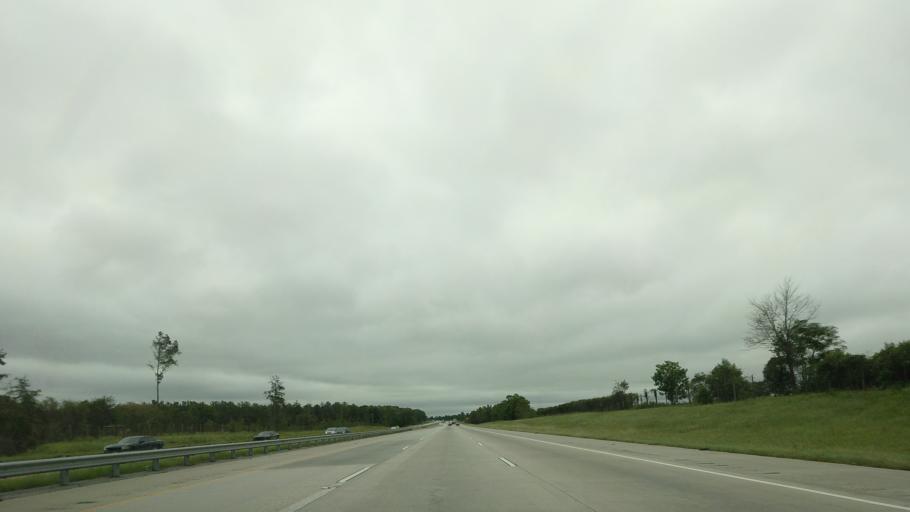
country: US
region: Georgia
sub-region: Dooly County
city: Unadilla
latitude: 32.3064
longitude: -83.7625
